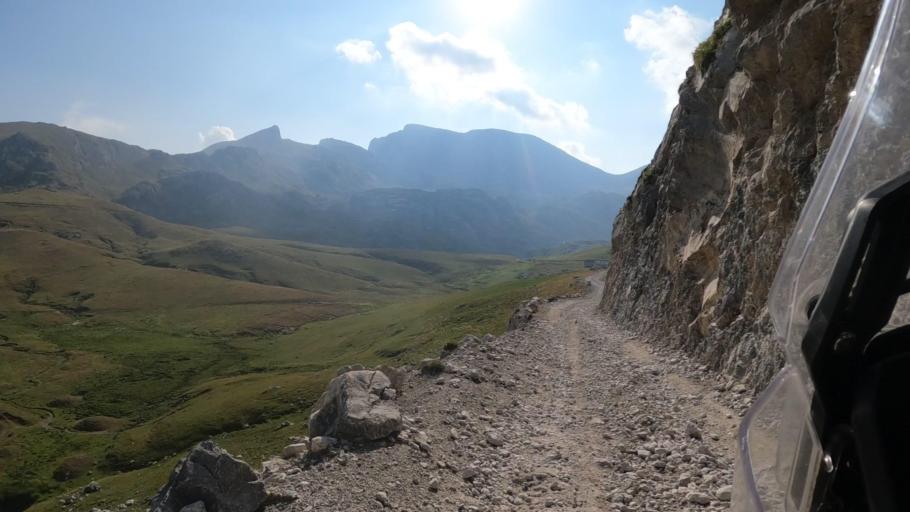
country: IT
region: Piedmont
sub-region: Provincia di Cuneo
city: Limone Piemonte
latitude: 44.1700
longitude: 7.6573
